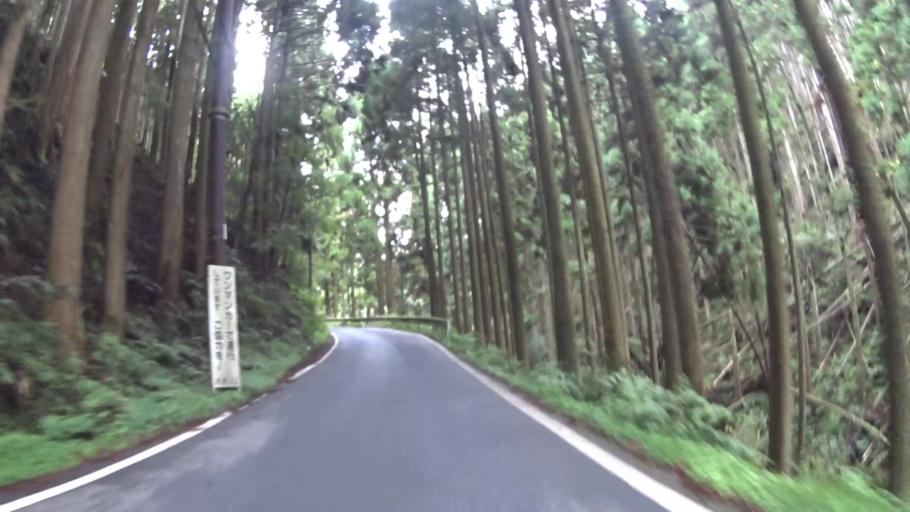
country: JP
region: Kyoto
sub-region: Kyoto-shi
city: Kamigyo-ku
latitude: 35.1199
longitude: 135.7759
